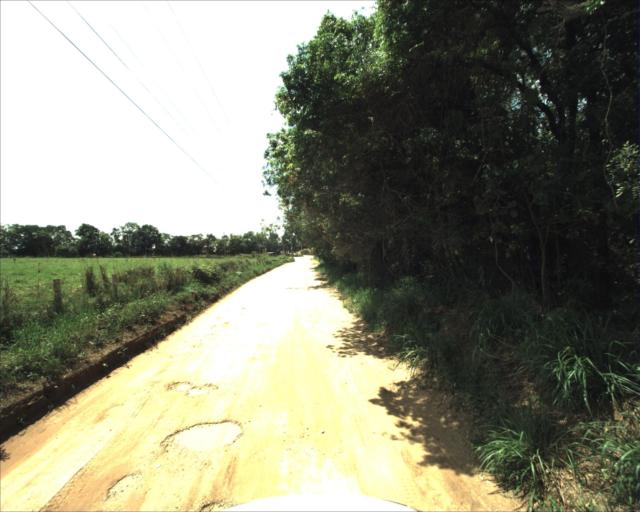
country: BR
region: Sao Paulo
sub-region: Aracoiaba Da Serra
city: Aracoiaba da Serra
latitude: -23.5535
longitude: -47.5458
